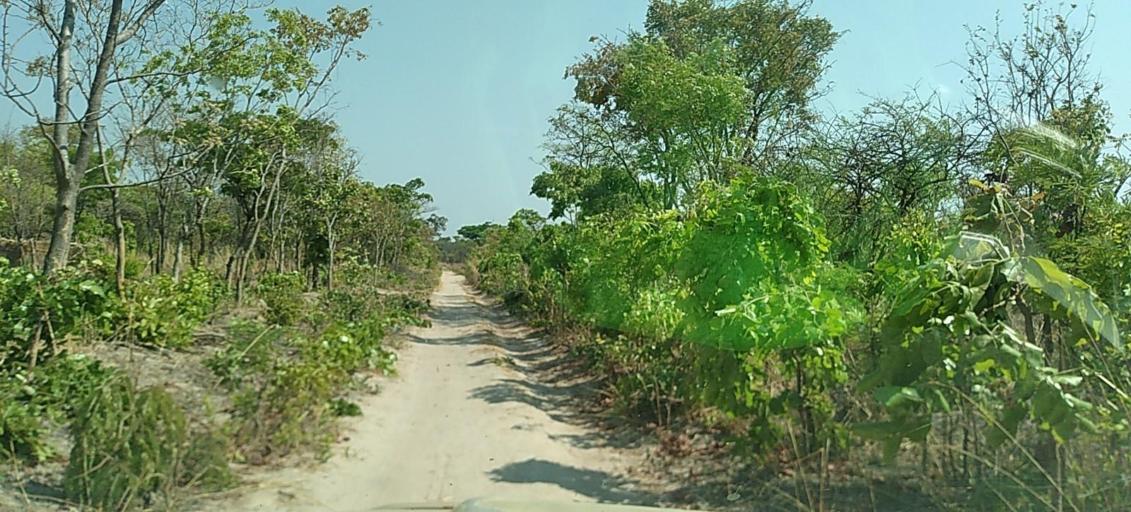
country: ZM
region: North-Western
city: Kalengwa
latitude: -13.3138
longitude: 24.8132
